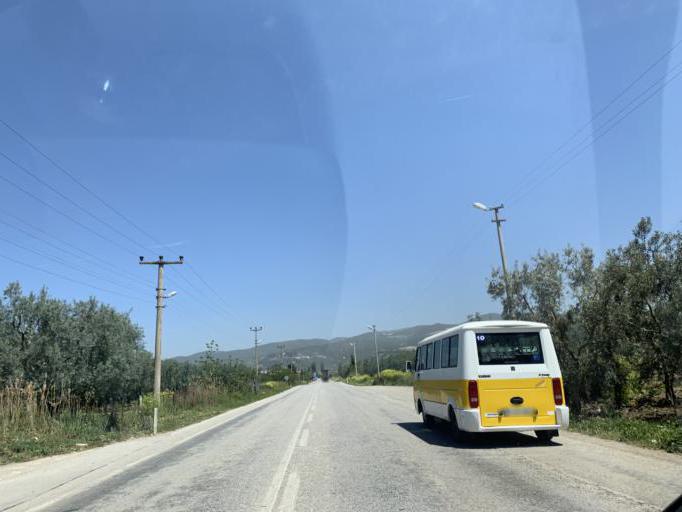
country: TR
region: Bursa
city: Iznik
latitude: 40.4157
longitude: 29.7131
